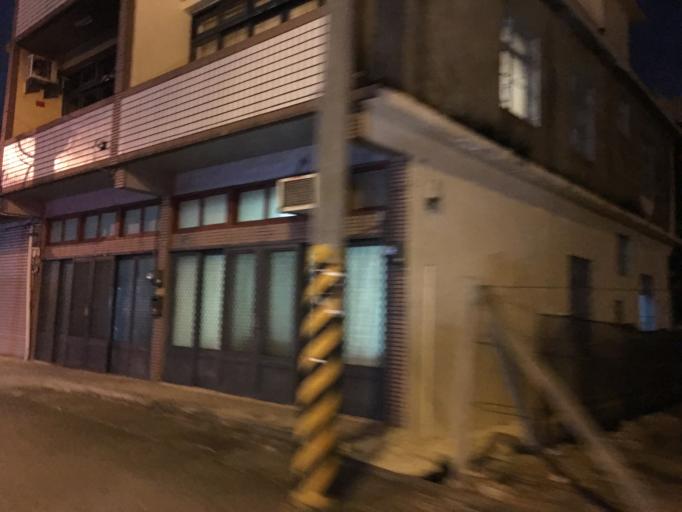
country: TW
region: Taiwan
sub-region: Hsinchu
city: Hsinchu
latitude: 24.7110
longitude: 120.9000
